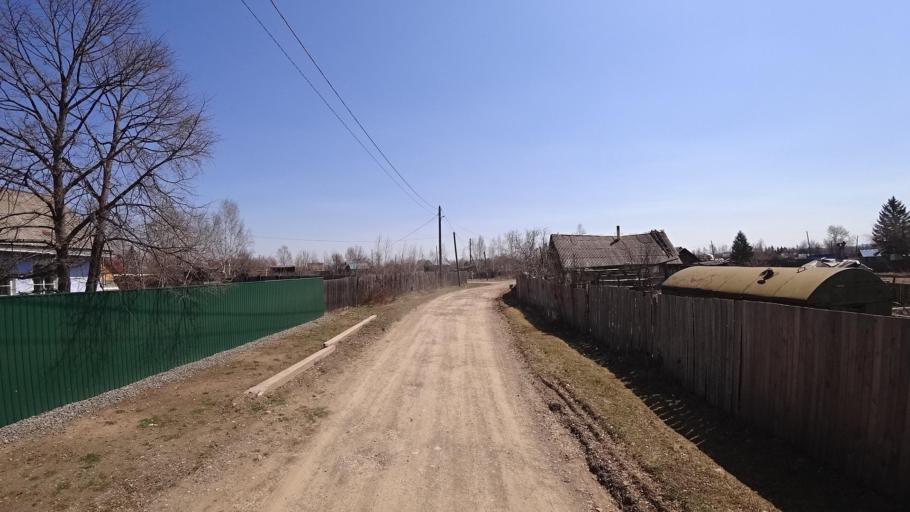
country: RU
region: Khabarovsk Krai
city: Khurba
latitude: 50.4111
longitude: 136.8670
